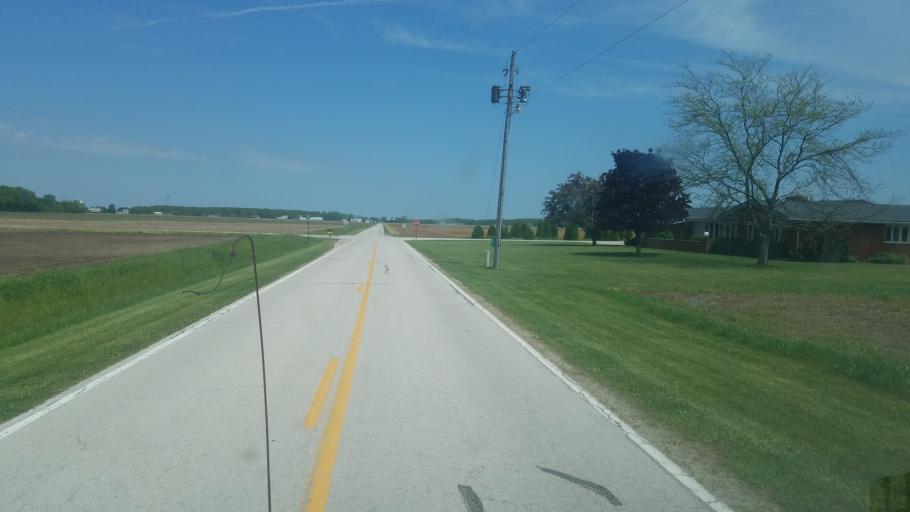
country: US
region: Ohio
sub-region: Ottawa County
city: Oak Harbor
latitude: 41.4574
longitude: -83.2017
